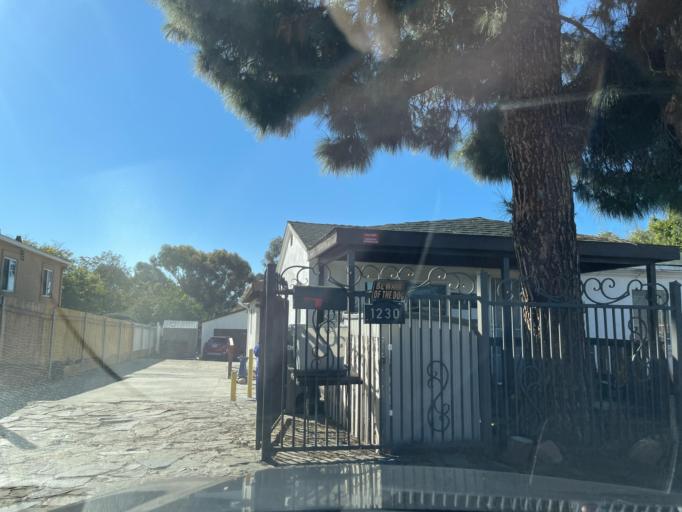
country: US
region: California
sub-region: San Diego County
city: National City
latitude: 32.6761
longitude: -117.0905
